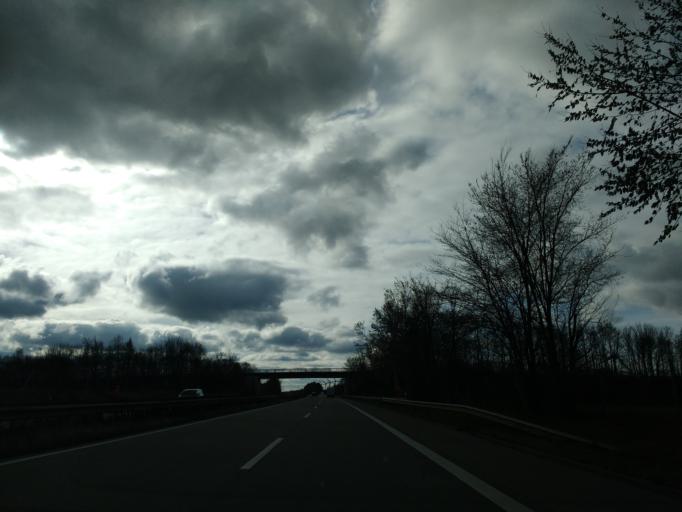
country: DE
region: Lower Saxony
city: Midlum
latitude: 53.7312
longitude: 8.6617
